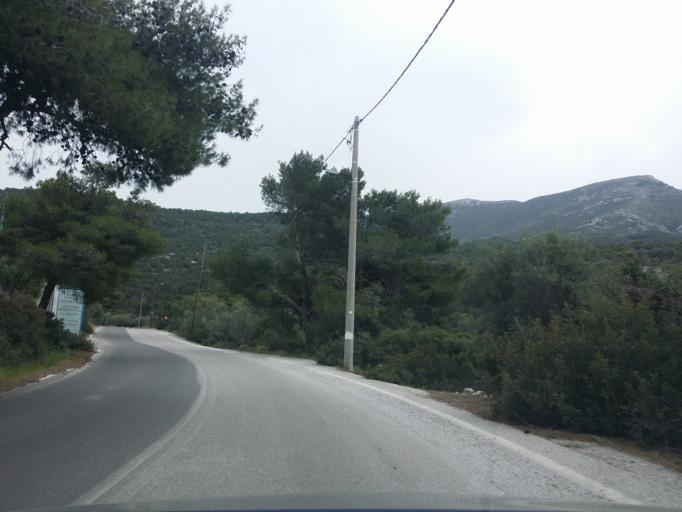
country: GR
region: Central Greece
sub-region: Nomos Voiotias
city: Kaparellion
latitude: 38.1488
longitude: 23.2314
